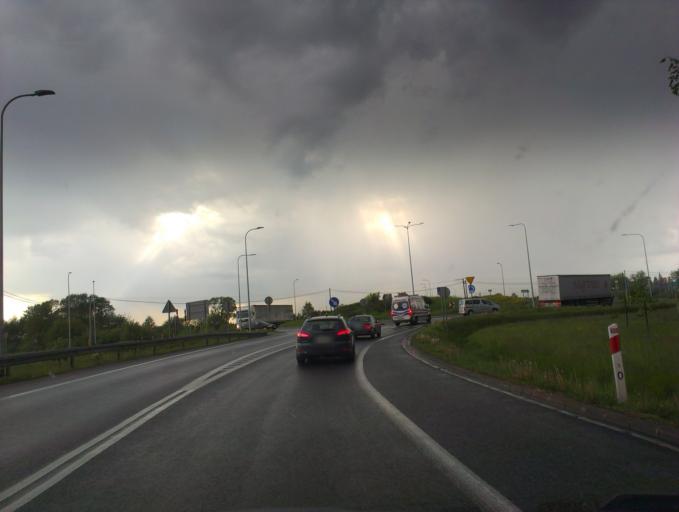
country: PL
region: Masovian Voivodeship
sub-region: Powiat zyrardowski
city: Mszczonow
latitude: 51.9810
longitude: 20.5283
